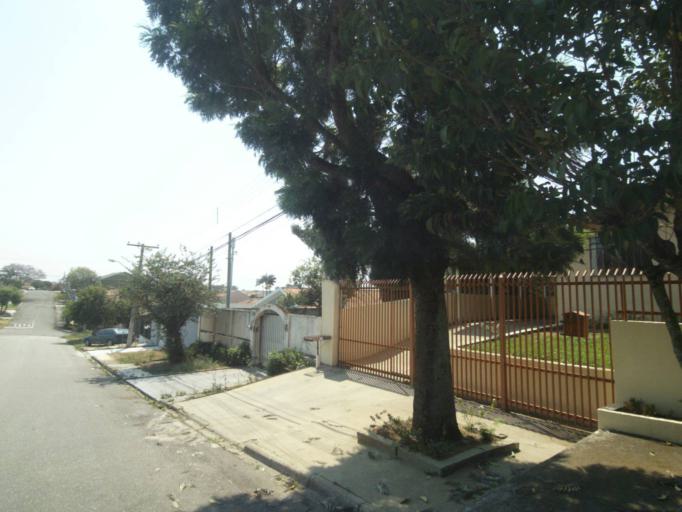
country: BR
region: Parana
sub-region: Sao Jose Dos Pinhais
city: Sao Jose dos Pinhais
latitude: -25.5066
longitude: -49.2719
